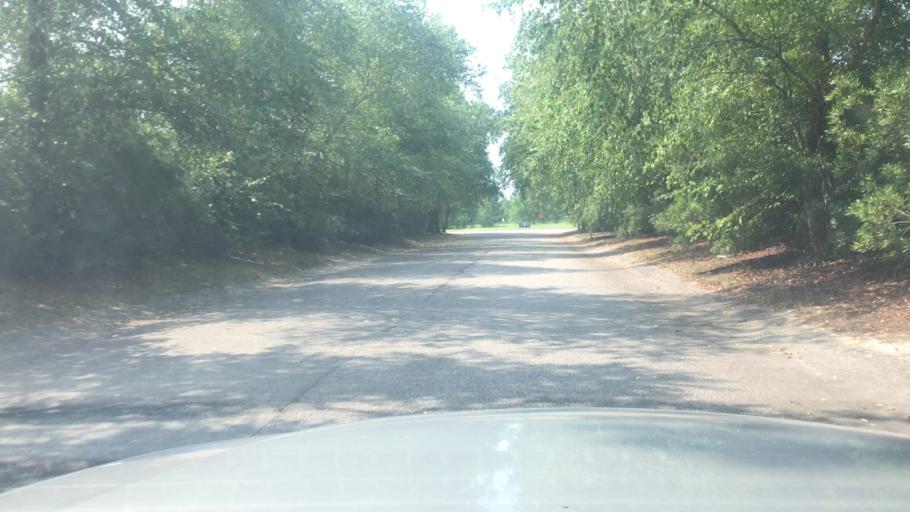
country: US
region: North Carolina
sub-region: Cumberland County
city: Hope Mills
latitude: 34.9981
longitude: -78.9523
